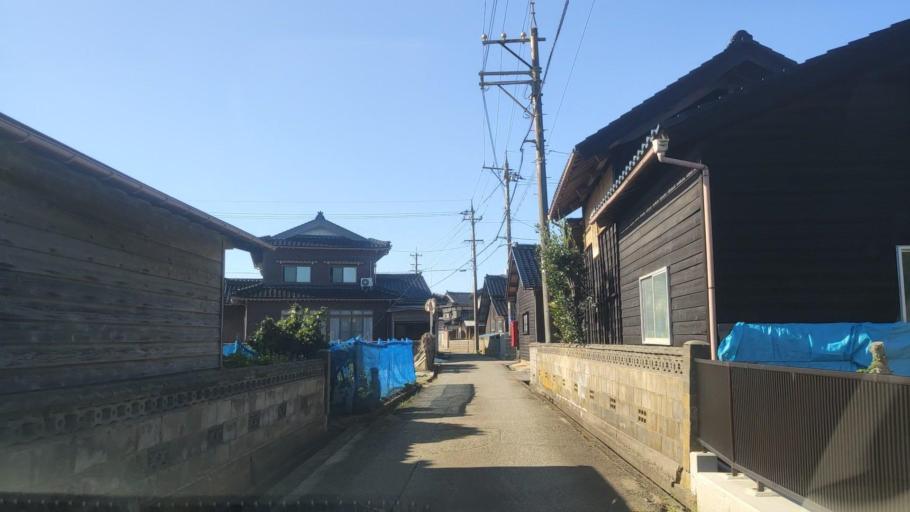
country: JP
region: Ishikawa
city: Hakui
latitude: 36.9499
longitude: 136.7624
